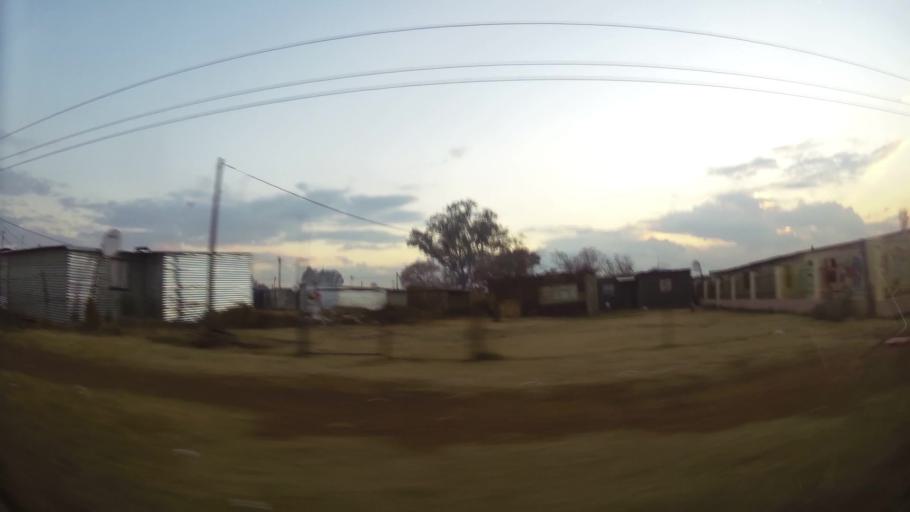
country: ZA
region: Gauteng
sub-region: City of Johannesburg Metropolitan Municipality
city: Orange Farm
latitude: -26.5524
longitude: 27.8600
